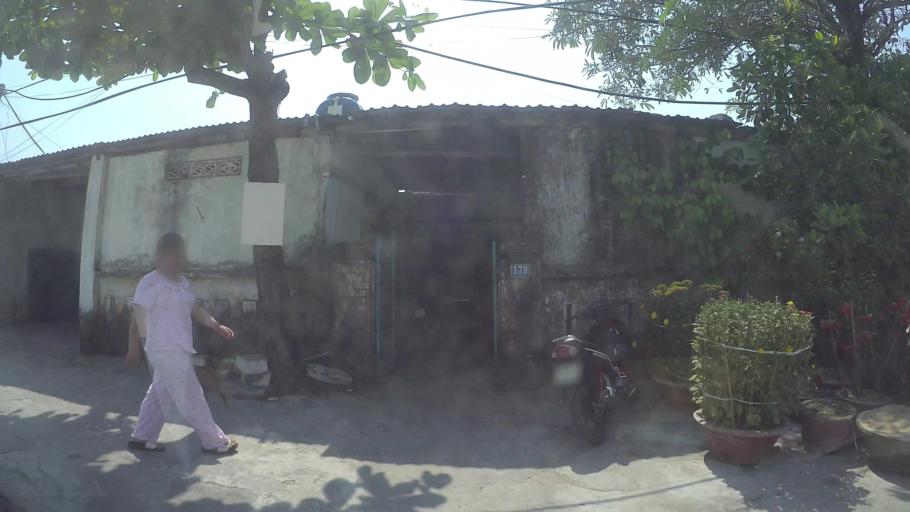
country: VN
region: Da Nang
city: Ngu Hanh Son
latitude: 16.0025
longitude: 108.2660
